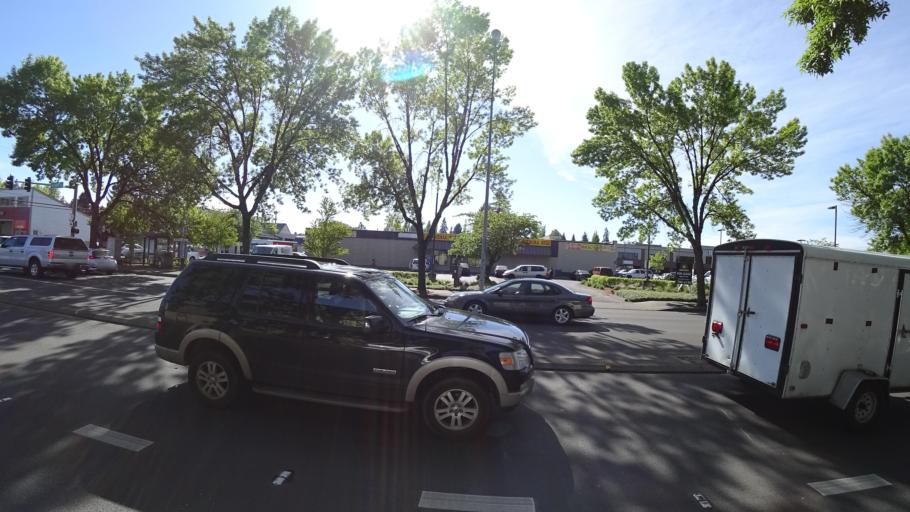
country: US
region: Oregon
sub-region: Washington County
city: Hillsboro
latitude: 45.5178
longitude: -122.9739
